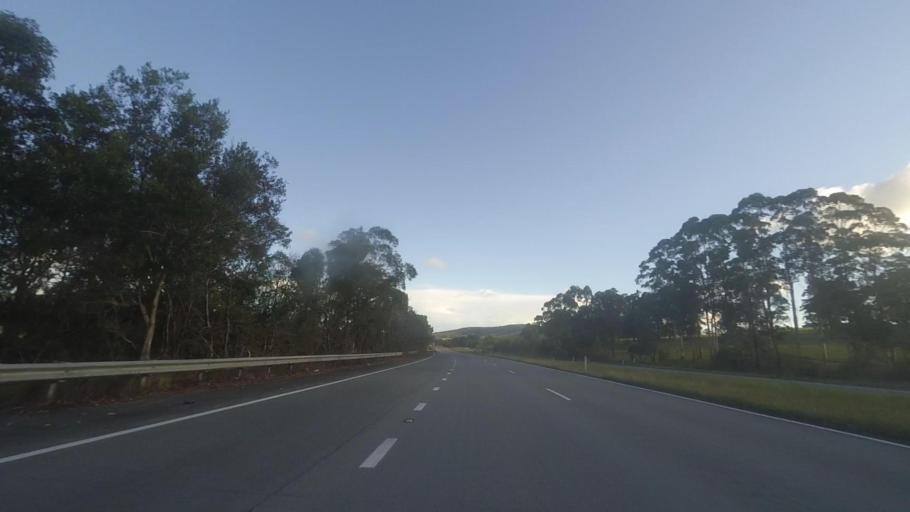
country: AU
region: New South Wales
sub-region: Great Lakes
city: Nabiac
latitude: -32.2535
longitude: 152.3237
